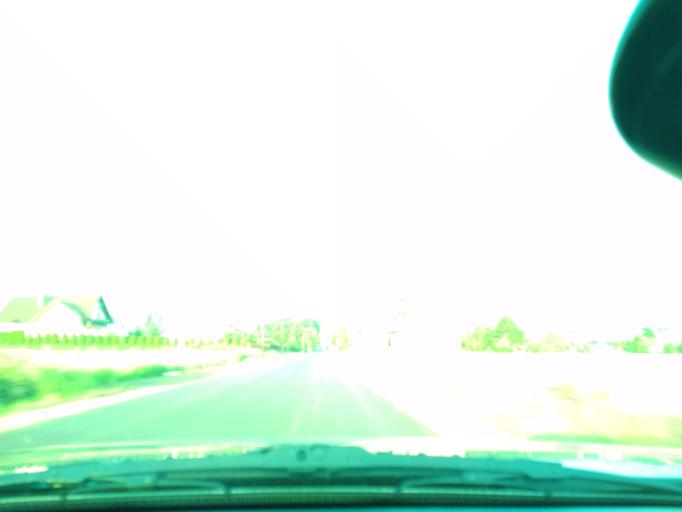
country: PL
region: Lesser Poland Voivodeship
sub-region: Powiat olkuski
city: Wolbrom
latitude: 50.4080
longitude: 19.7828
